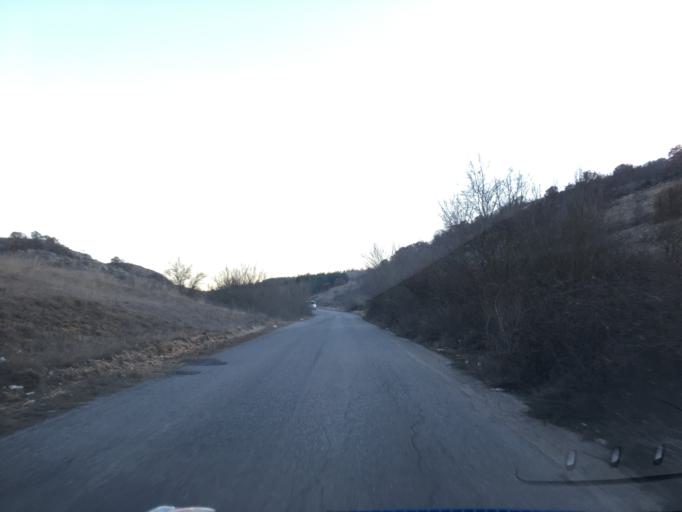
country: GR
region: West Macedonia
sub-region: Nomos Kozanis
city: Koila
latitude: 40.3284
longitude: 21.8120
